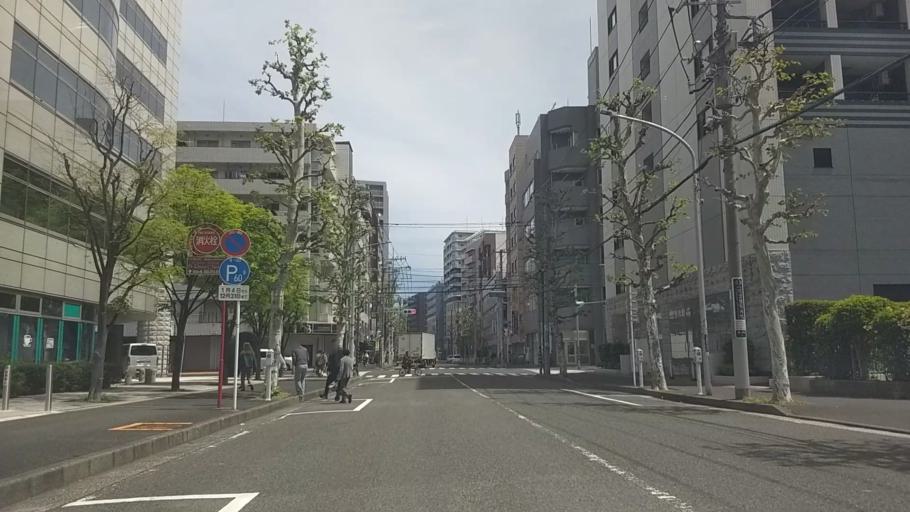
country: JP
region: Kanagawa
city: Yokohama
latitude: 35.4392
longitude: 139.6317
